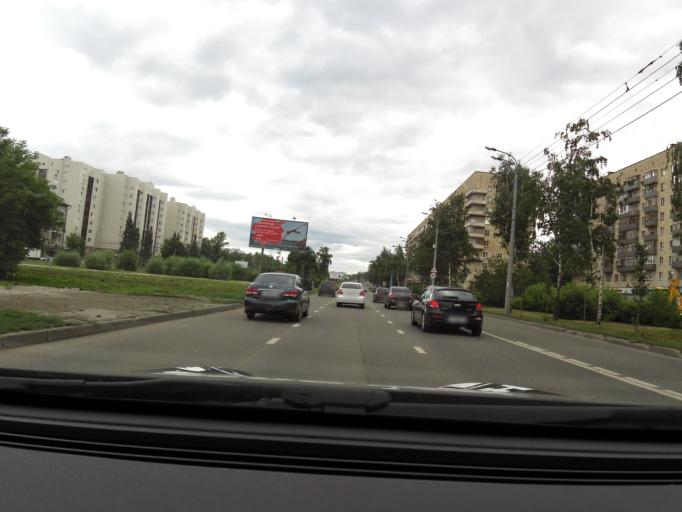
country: RU
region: Tatarstan
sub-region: Gorod Kazan'
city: Kazan
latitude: 55.8199
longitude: 49.0540
